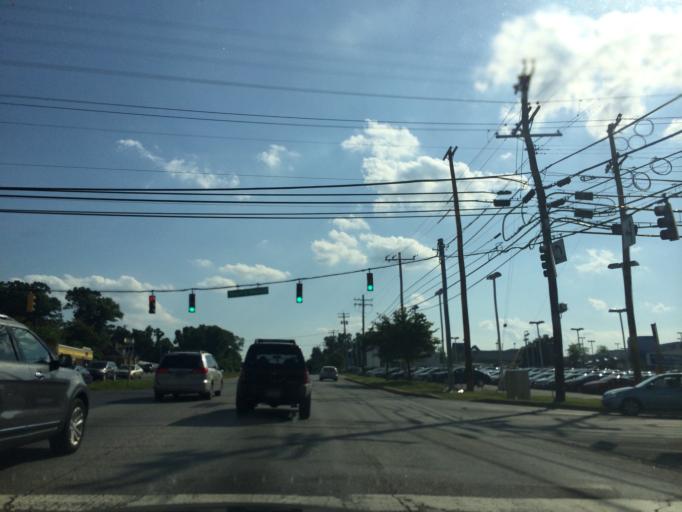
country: US
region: Maryland
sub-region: Howard County
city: Ellicott City
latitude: 39.2830
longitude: -76.8103
